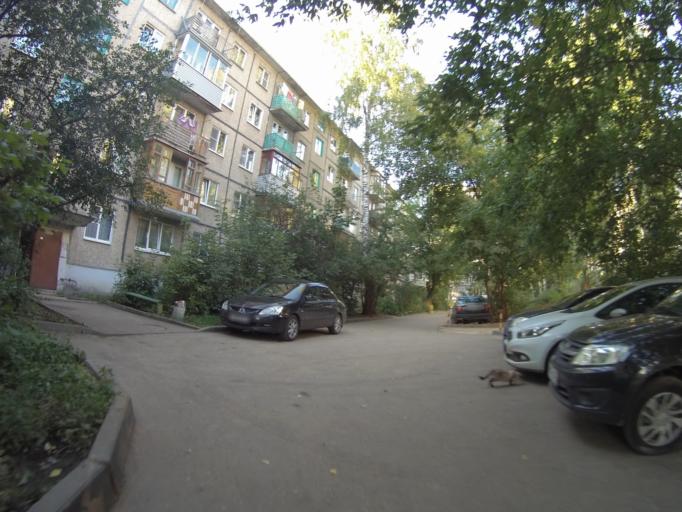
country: RU
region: Vladimir
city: Vladimir
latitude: 56.1473
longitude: 40.3629
